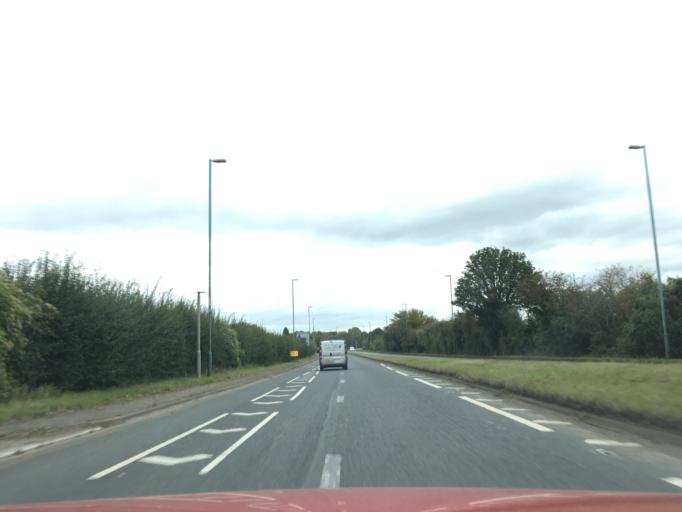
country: GB
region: England
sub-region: Gloucestershire
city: Stonehouse
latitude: 51.7620
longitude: -2.3342
